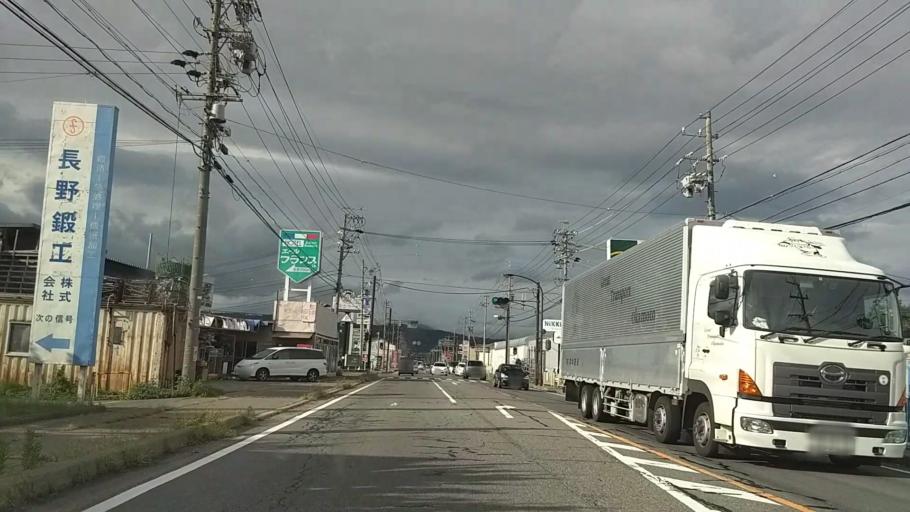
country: JP
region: Nagano
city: Suzaka
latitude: 36.6825
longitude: 138.2678
